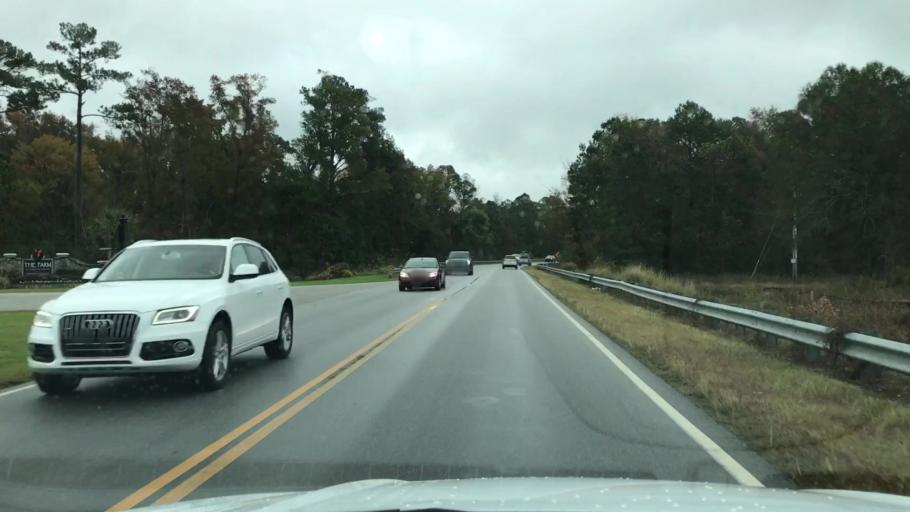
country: US
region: South Carolina
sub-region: Horry County
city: Myrtle Beach
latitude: 33.7548
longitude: -78.8755
